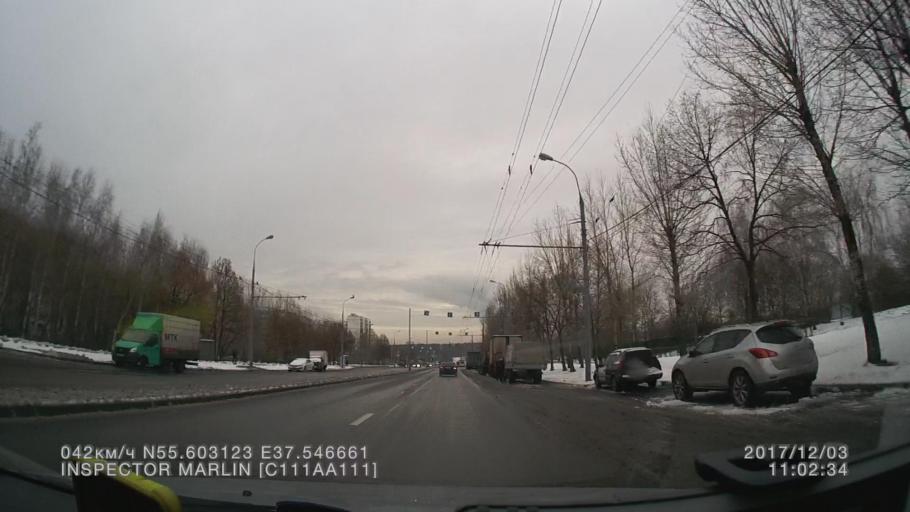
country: RU
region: Moscow
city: Yasenevo
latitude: 55.6031
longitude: 37.5467
